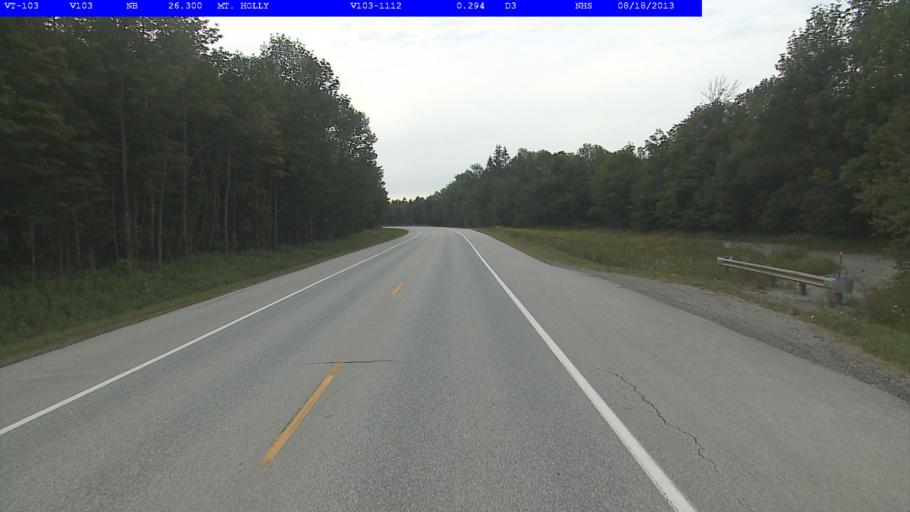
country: US
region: Vermont
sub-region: Windsor County
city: Chester
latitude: 43.4362
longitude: -72.7385
